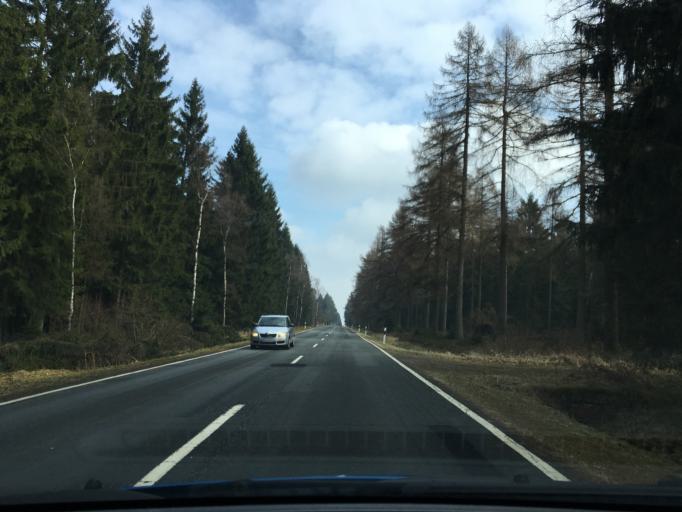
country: DE
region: Lower Saxony
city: Heinade
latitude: 51.7742
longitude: 9.5864
